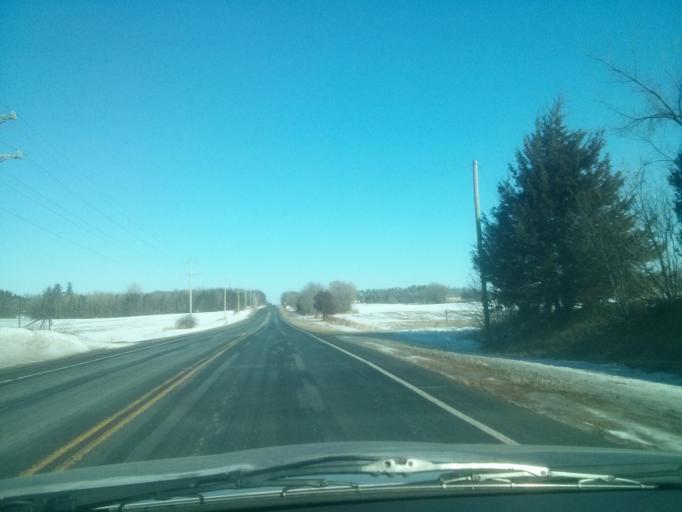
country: US
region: Minnesota
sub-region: Washington County
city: Bayport
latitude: 45.0750
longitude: -92.7361
